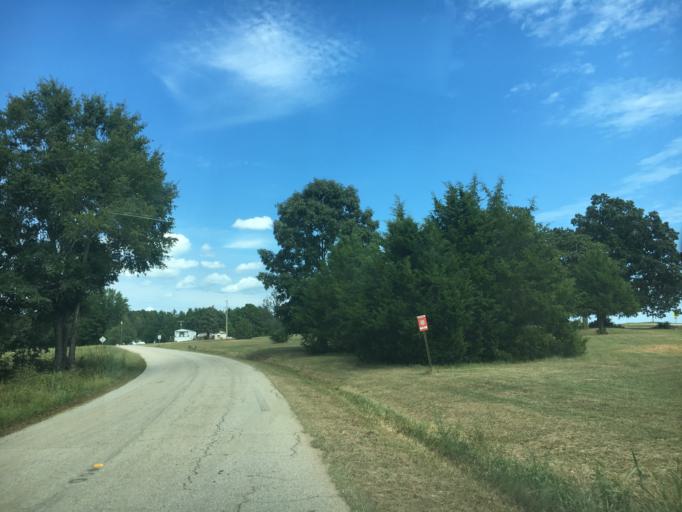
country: US
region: South Carolina
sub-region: Laurens County
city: Watts Mills
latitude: 34.5087
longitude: -81.9481
